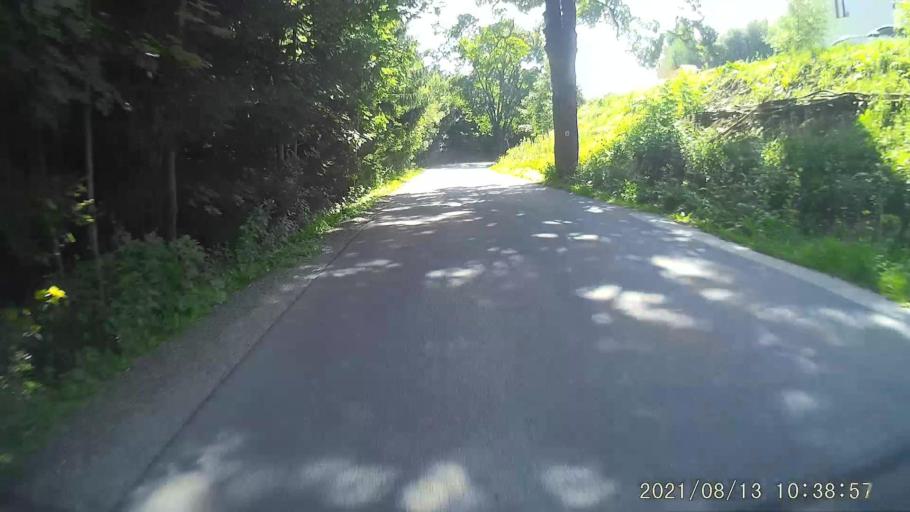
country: PL
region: Lower Silesian Voivodeship
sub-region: Powiat klodzki
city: Duszniki-Zdroj
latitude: 50.4429
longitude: 16.3445
